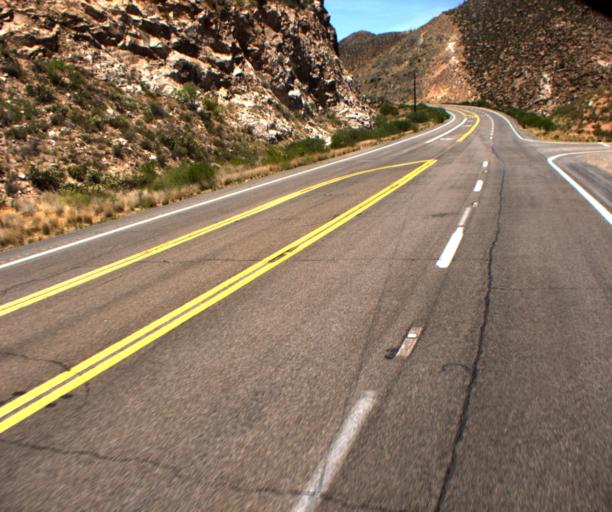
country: US
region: Arizona
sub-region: Gila County
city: Claypool
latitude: 33.5196
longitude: -110.8712
